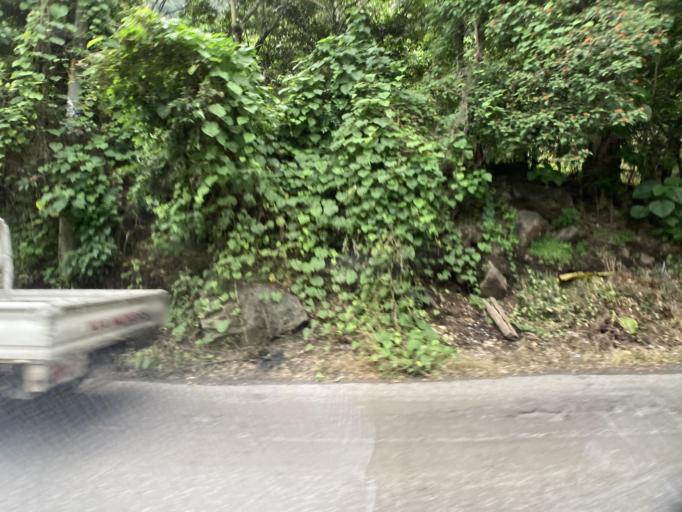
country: GT
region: Guatemala
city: Villa Canales
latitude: 14.4238
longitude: -90.5346
